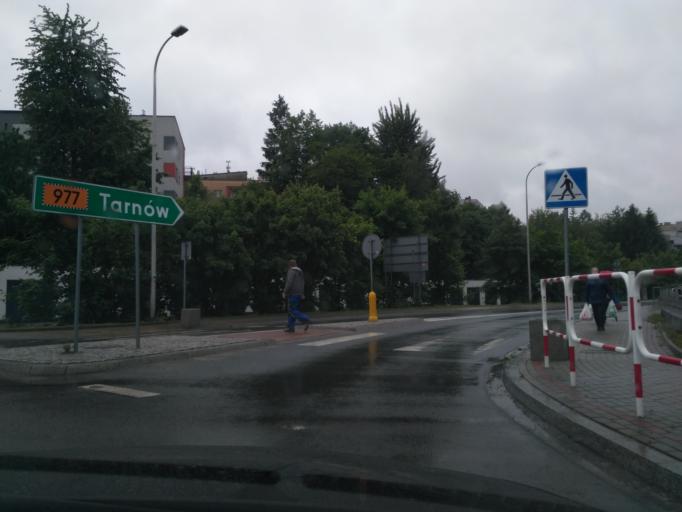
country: PL
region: Lesser Poland Voivodeship
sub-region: Powiat gorlicki
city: Gorlice
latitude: 49.6618
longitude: 21.1577
